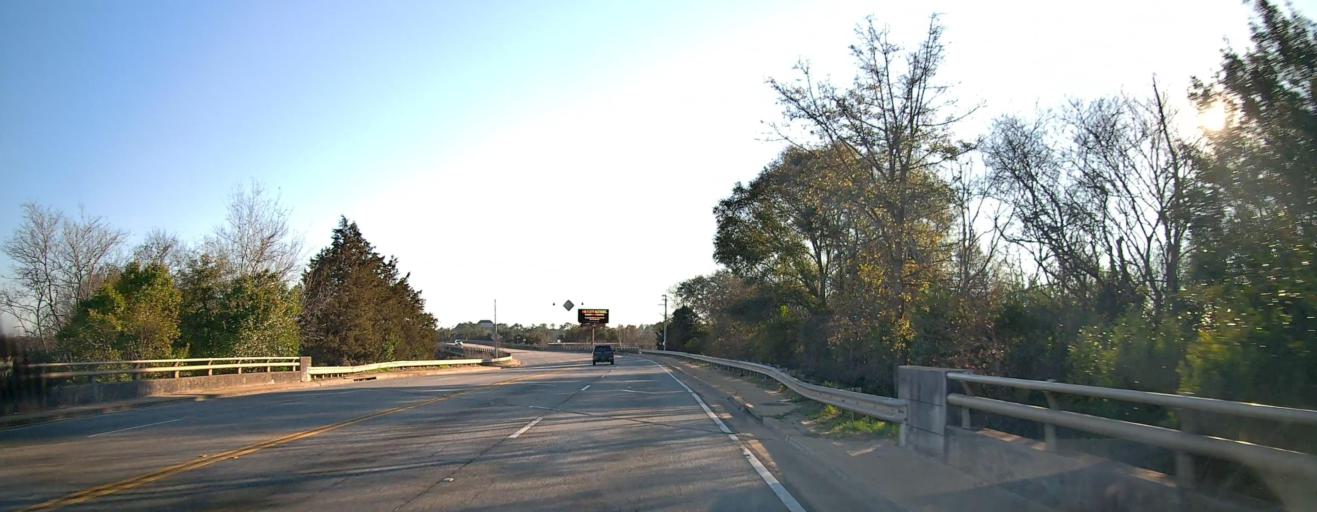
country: US
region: Georgia
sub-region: Dougherty County
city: Albany
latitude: 31.6040
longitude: -84.1558
